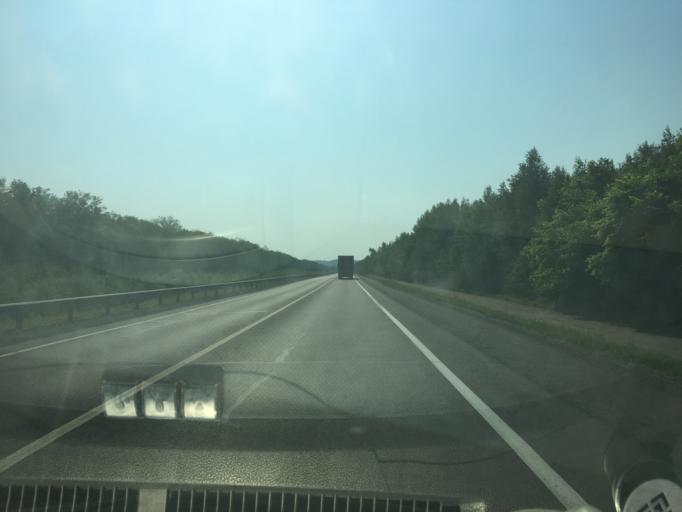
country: RU
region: Nizjnij Novgorod
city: Kstovo
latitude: 56.0876
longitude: 44.3402
